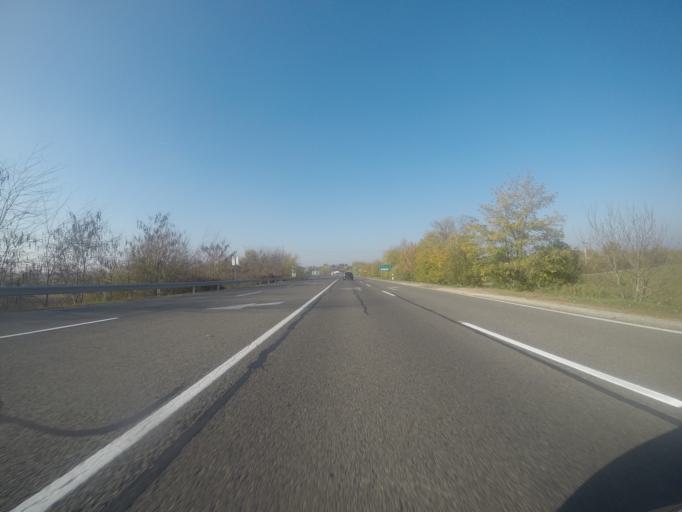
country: HU
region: Fejer
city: Ercsi
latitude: 47.2352
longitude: 18.8907
